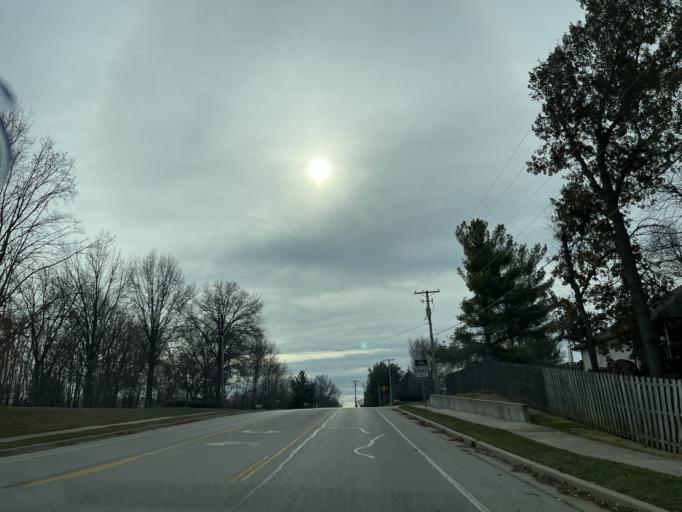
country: US
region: Illinois
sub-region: Sangamon County
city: Leland Grove
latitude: 39.7929
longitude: -89.7297
